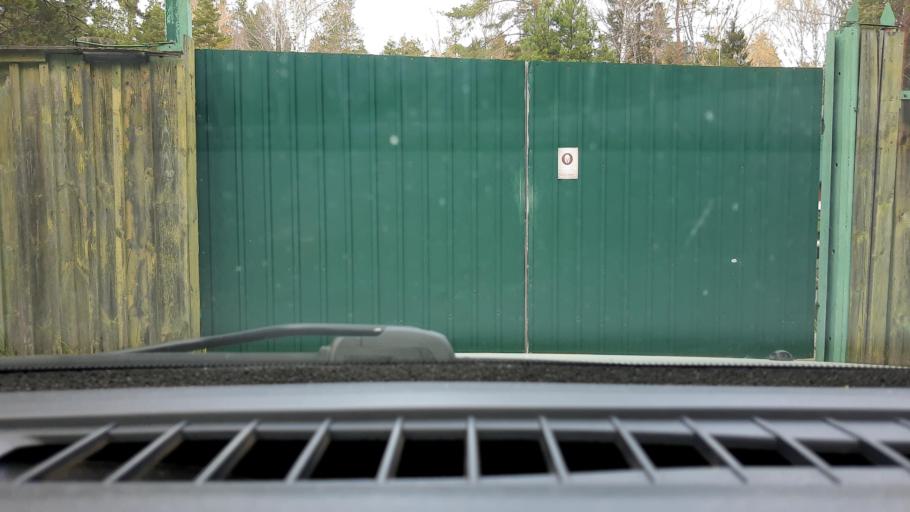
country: RU
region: Nizjnij Novgorod
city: Kstovo
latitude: 56.1710
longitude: 44.1328
